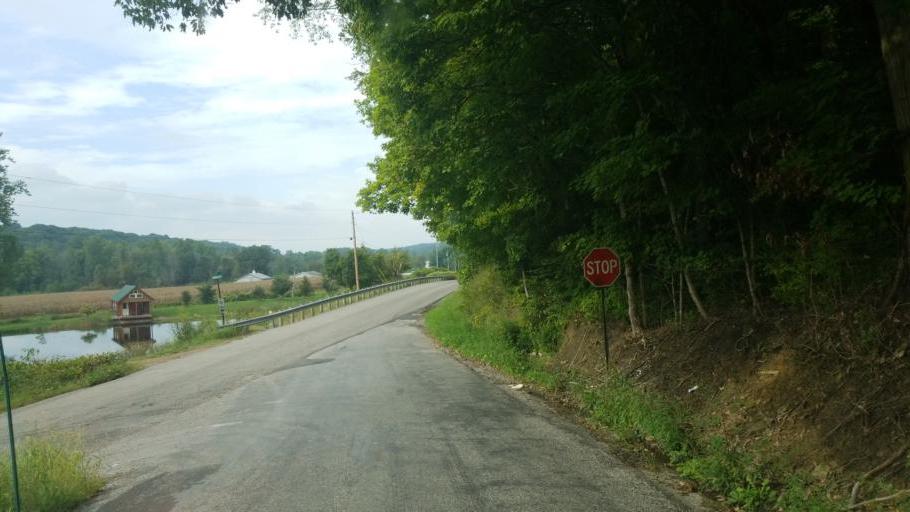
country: US
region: Ohio
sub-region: Wayne County
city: Wooster
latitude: 40.9024
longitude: -82.0072
